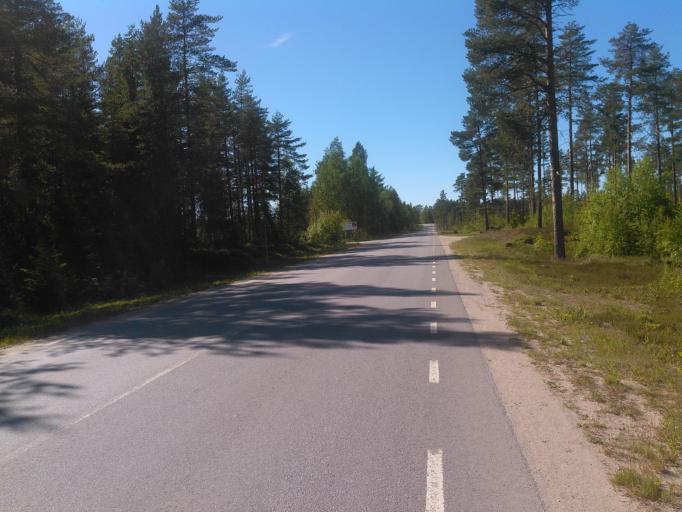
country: SE
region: Vaesterbotten
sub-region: Umea Kommun
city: Roback
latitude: 63.8249
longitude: 20.1754
